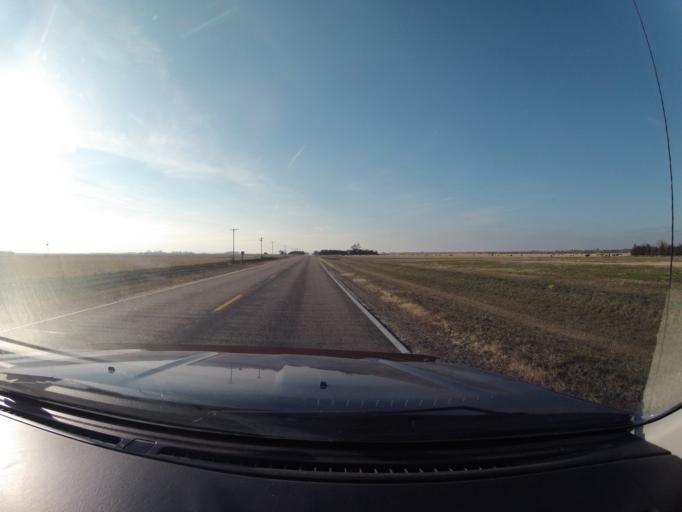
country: US
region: Nebraska
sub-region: Buffalo County
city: Kearney
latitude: 40.6410
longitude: -99.0161
